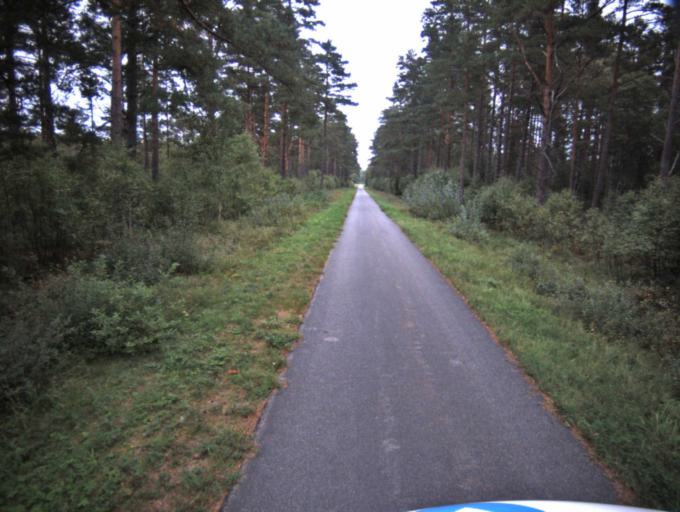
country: SE
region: Vaestra Goetaland
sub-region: Ulricehamns Kommun
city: Ulricehamn
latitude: 57.9467
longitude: 13.5014
